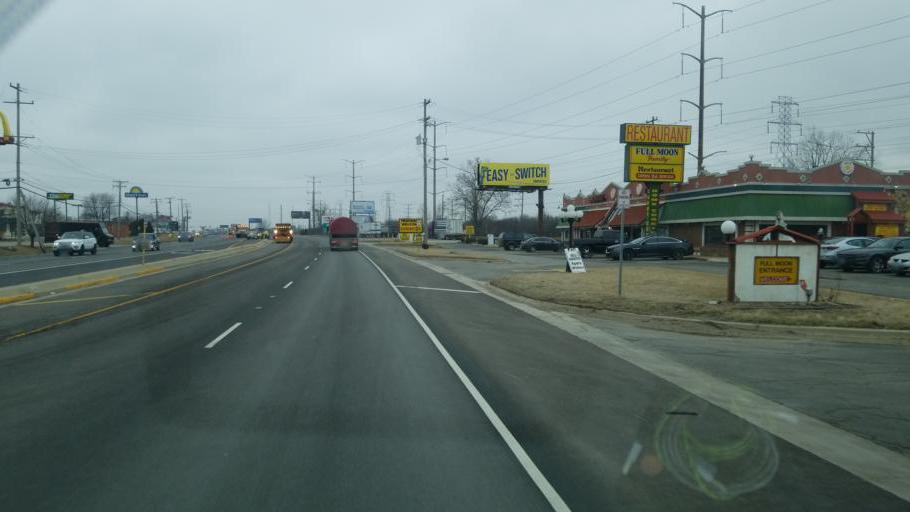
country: US
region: Illinois
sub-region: Lake County
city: Knollwood
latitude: 42.3033
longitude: -87.8755
